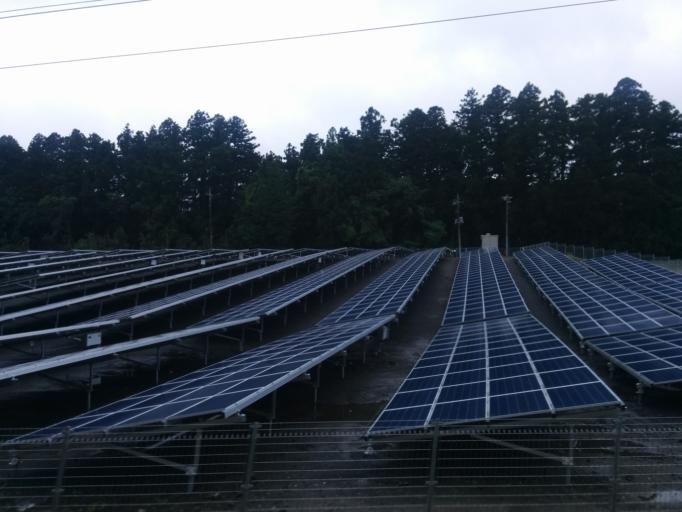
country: JP
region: Tochigi
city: Imaichi
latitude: 36.6637
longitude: 139.7226
